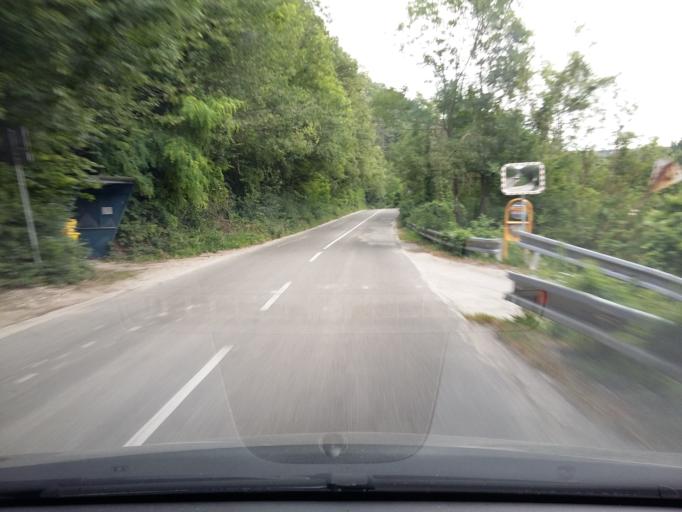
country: SK
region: Trnavsky
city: Smolenice
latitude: 48.5446
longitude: 17.4225
